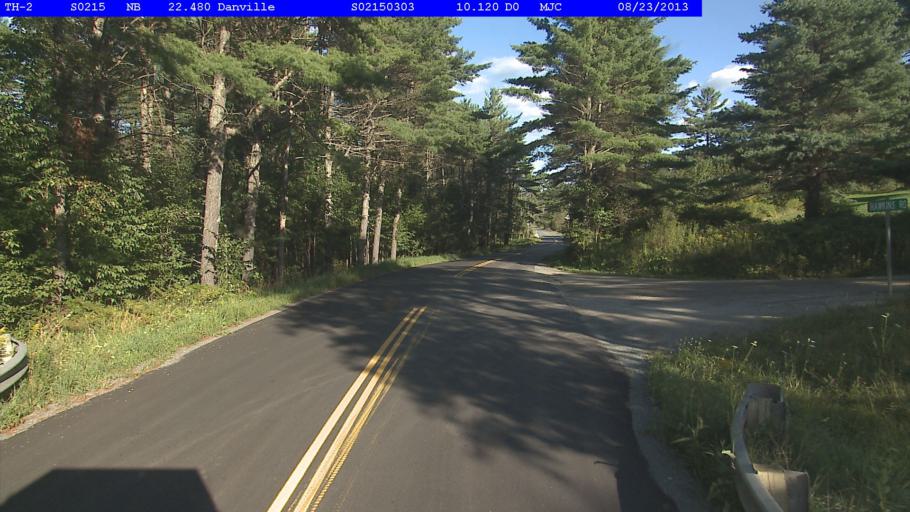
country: US
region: Vermont
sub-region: Caledonia County
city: St Johnsbury
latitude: 44.4491
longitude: -72.0638
